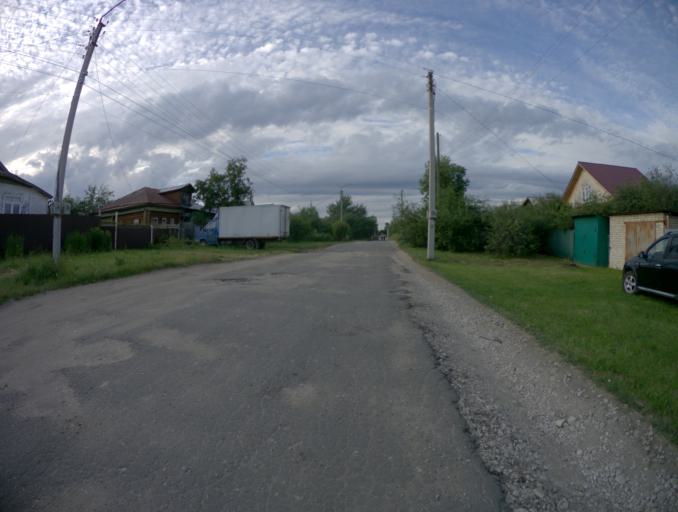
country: RU
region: Vladimir
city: Gorokhovets
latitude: 56.1972
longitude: 42.6809
